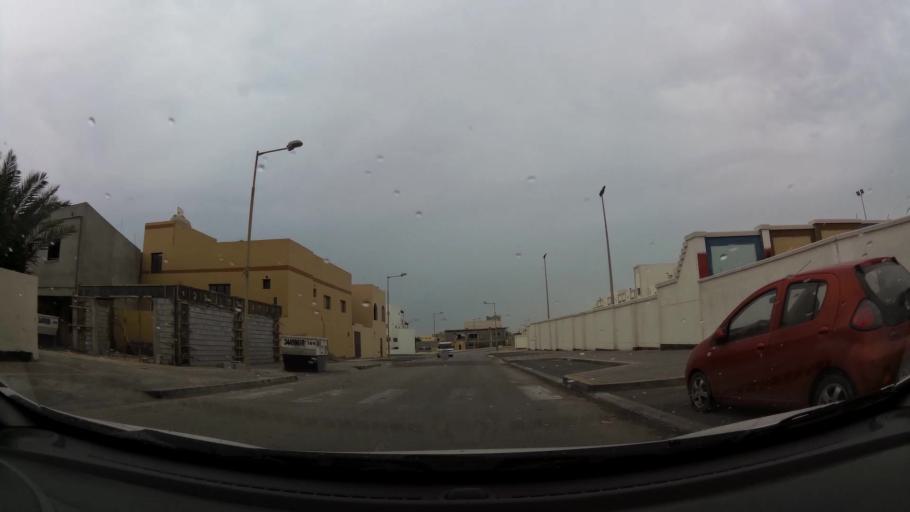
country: BH
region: Central Governorate
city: Madinat Hamad
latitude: 26.0988
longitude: 50.5029
